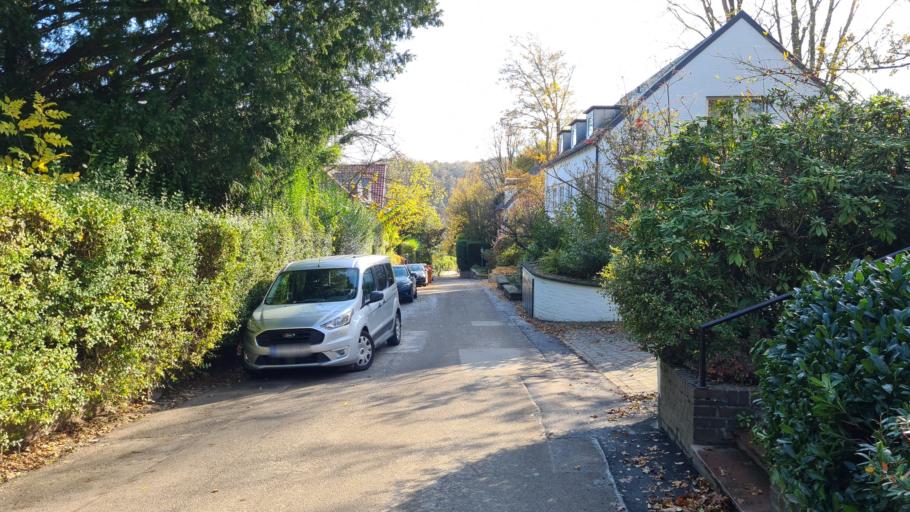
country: DE
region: North Rhine-Westphalia
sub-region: Regierungsbezirk Dusseldorf
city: Heiligenhaus
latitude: 51.3890
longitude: 6.9951
